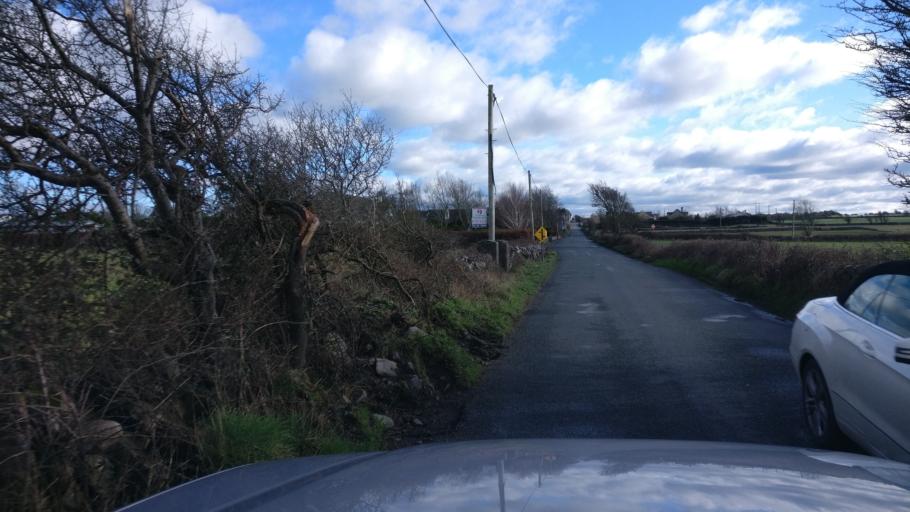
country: IE
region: Connaught
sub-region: County Galway
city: Oranmore
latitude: 53.2672
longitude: -8.8726
